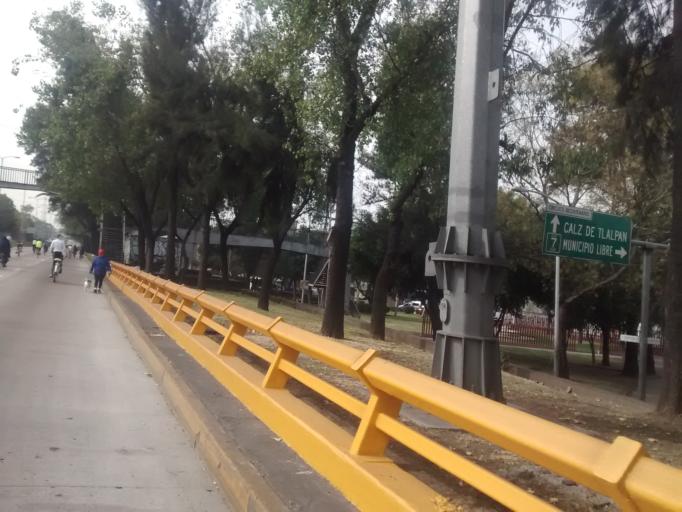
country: MX
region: Mexico City
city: Colonia Nativitas
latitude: 19.3660
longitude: -99.1269
